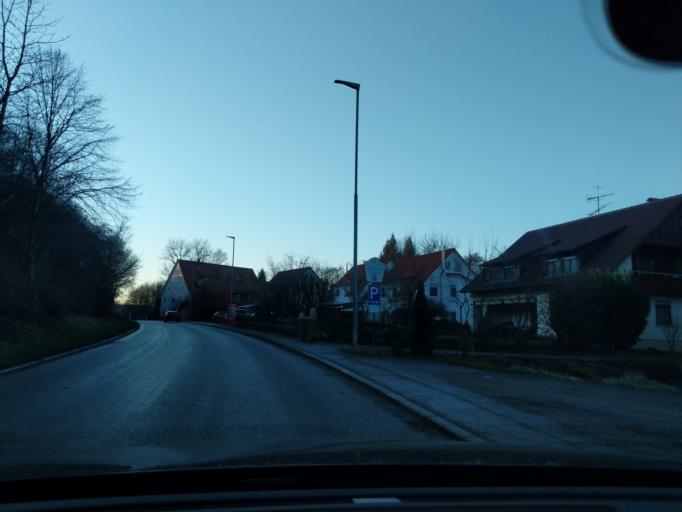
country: DE
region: Baden-Wuerttemberg
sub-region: Tuebingen Region
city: Salem
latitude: 47.7463
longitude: 9.2999
